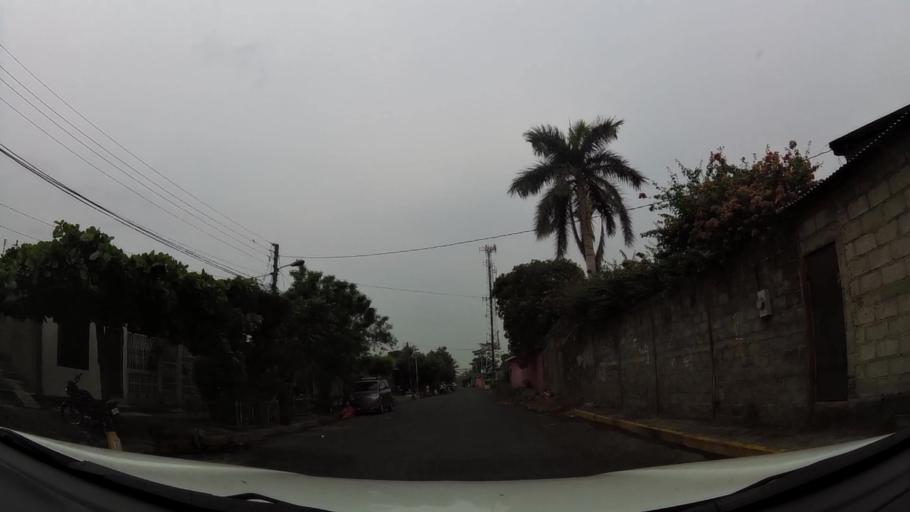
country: NI
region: Leon
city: Leon
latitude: 12.4488
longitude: -86.8730
